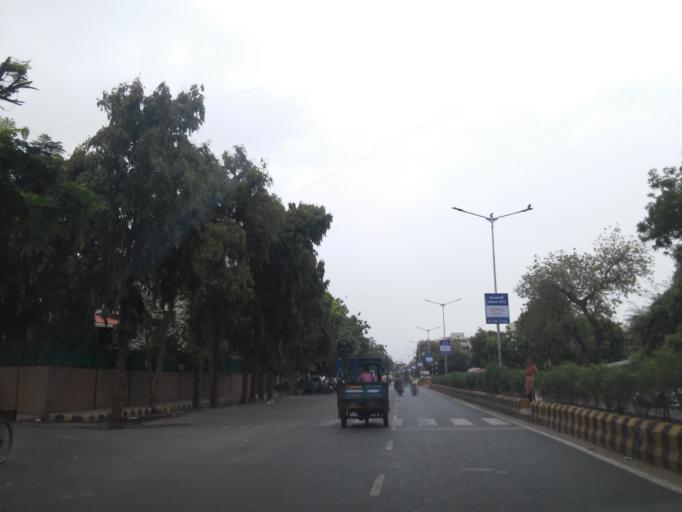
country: IN
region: Gujarat
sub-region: Ahmadabad
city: Ahmedabad
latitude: 23.0139
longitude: 72.5610
